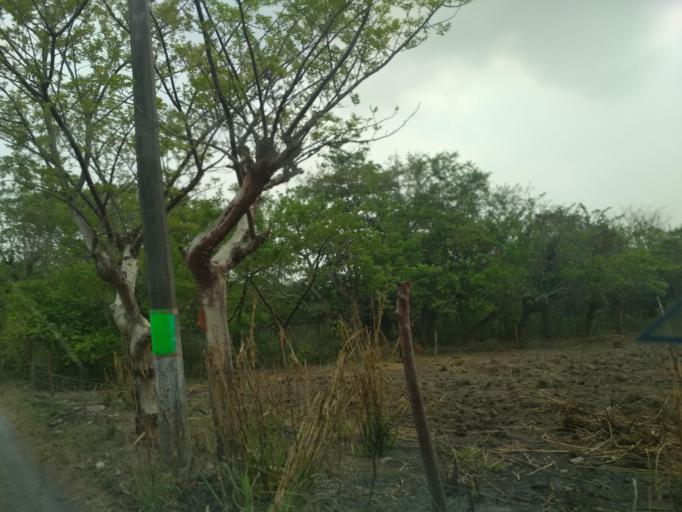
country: MX
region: Veracruz
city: Paso del Toro
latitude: 19.0250
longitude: -96.1495
